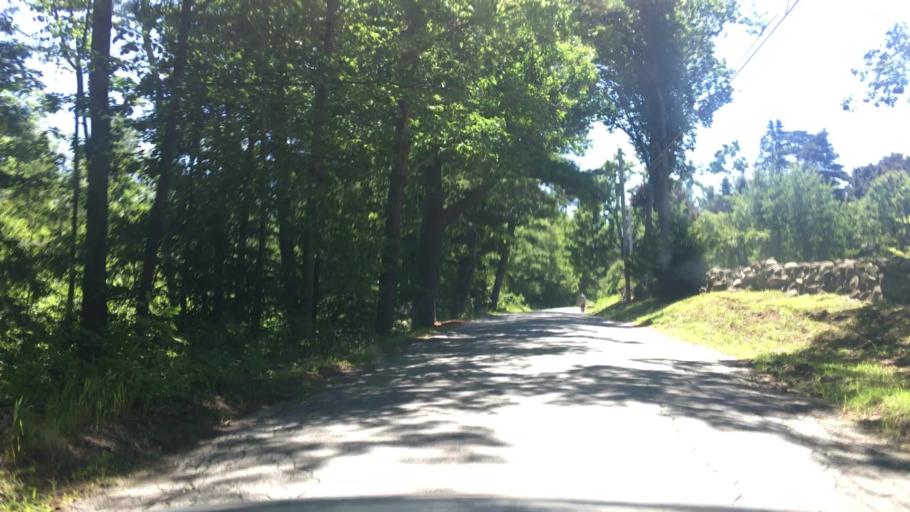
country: US
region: New Hampshire
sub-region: Merrimack County
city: Contoocook
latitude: 43.2263
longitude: -71.6805
